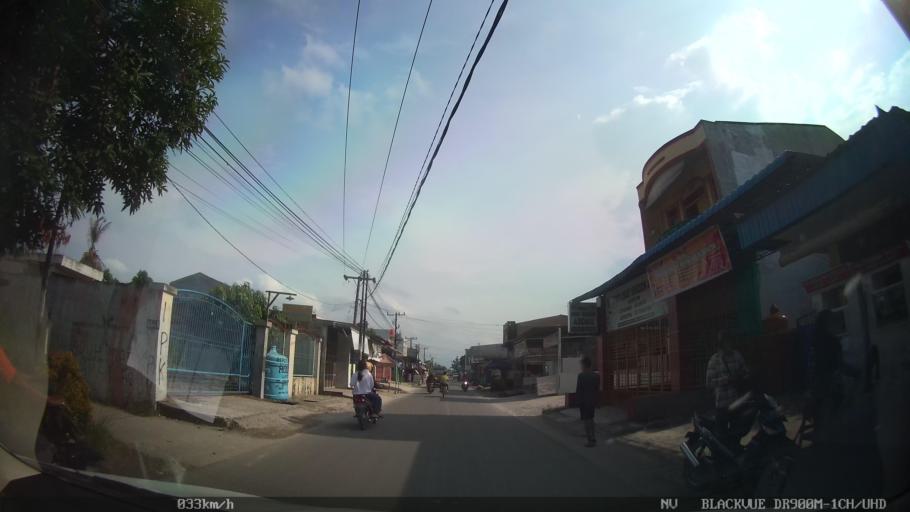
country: ID
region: North Sumatra
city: Medan
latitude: 3.5805
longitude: 98.7567
